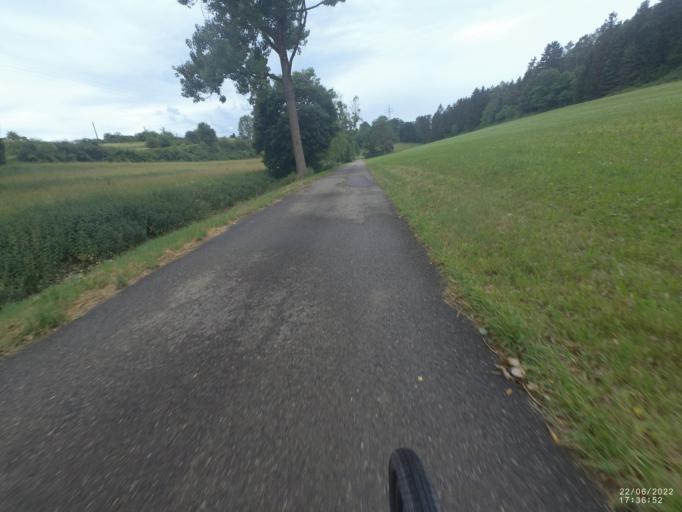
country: DE
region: Baden-Wuerttemberg
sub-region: Regierungsbezirk Stuttgart
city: Gerstetten
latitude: 48.6177
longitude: 10.0049
